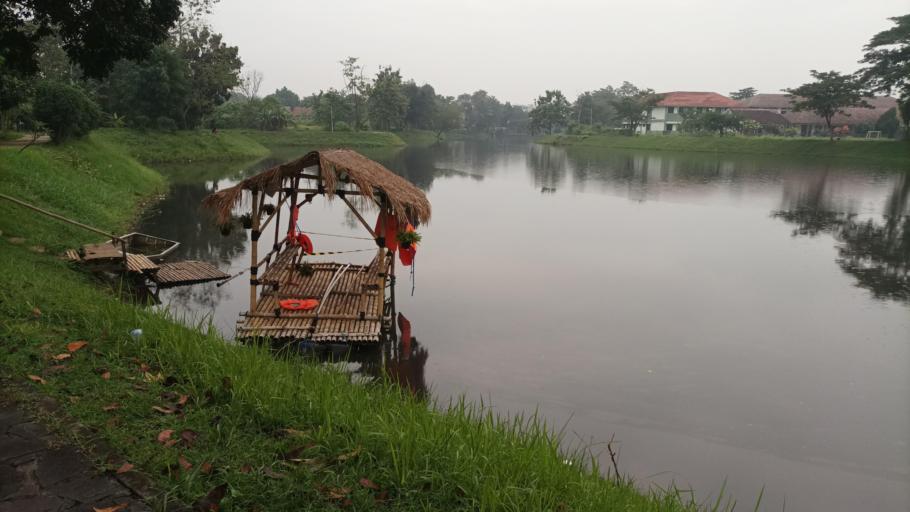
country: ID
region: West Java
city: Cileungsir
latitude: -6.3916
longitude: 106.9140
